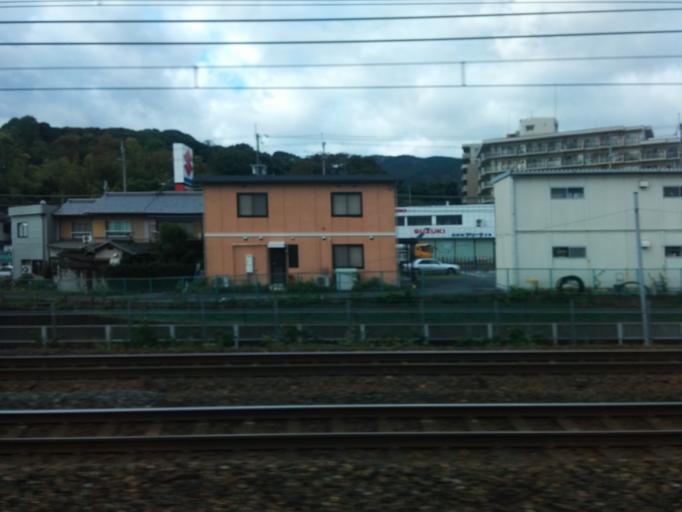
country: JP
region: Shiga Prefecture
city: Otsu-shi
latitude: 34.9927
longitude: 135.8861
